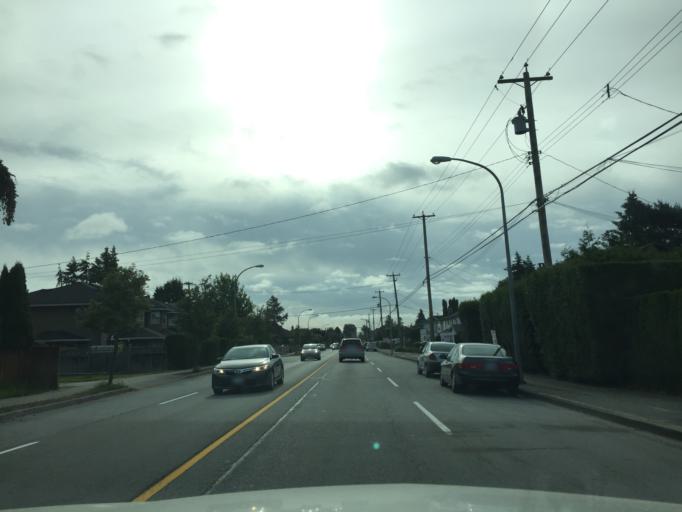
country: CA
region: British Columbia
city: Richmond
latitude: 49.1482
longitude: -123.1237
